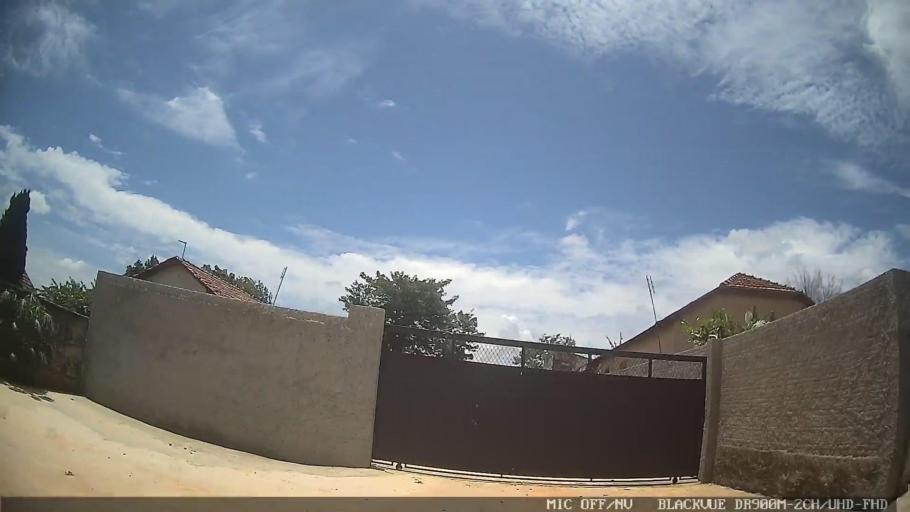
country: BR
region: Sao Paulo
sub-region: Laranjal Paulista
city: Laranjal Paulista
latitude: -23.0480
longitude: -47.8344
